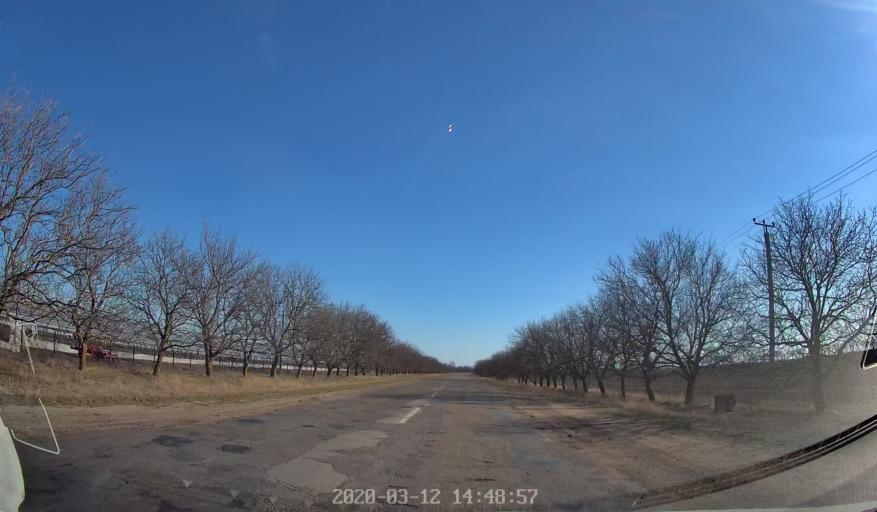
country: MD
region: Criuleni
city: Criuleni
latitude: 47.2280
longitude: 29.1424
